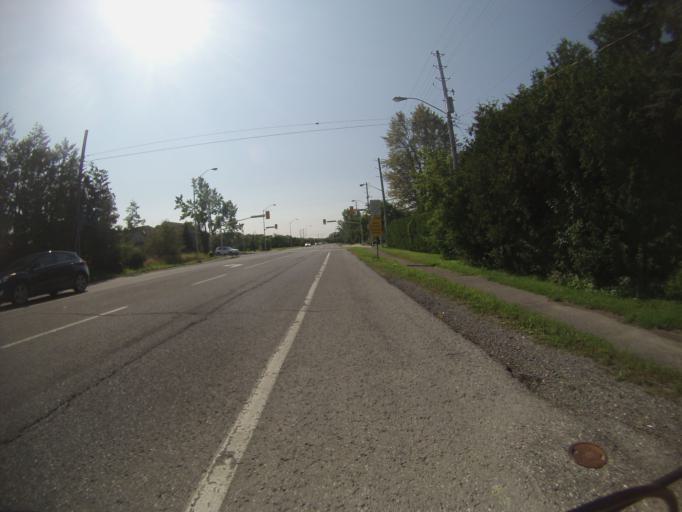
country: CA
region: Ontario
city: Ottawa
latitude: 45.3618
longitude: -75.7003
